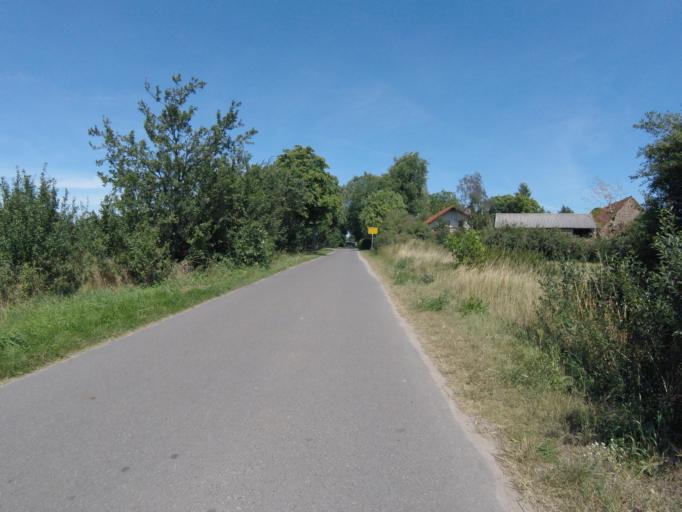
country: DE
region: Brandenburg
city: Mittenwalde
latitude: 52.2838
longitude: 13.5459
